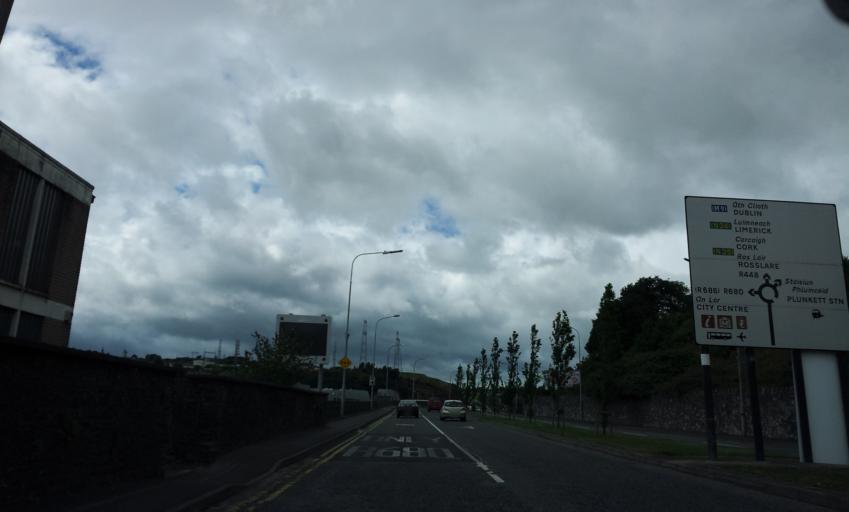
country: IE
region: Munster
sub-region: Waterford
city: Waterford
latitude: 52.2654
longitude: -7.1121
